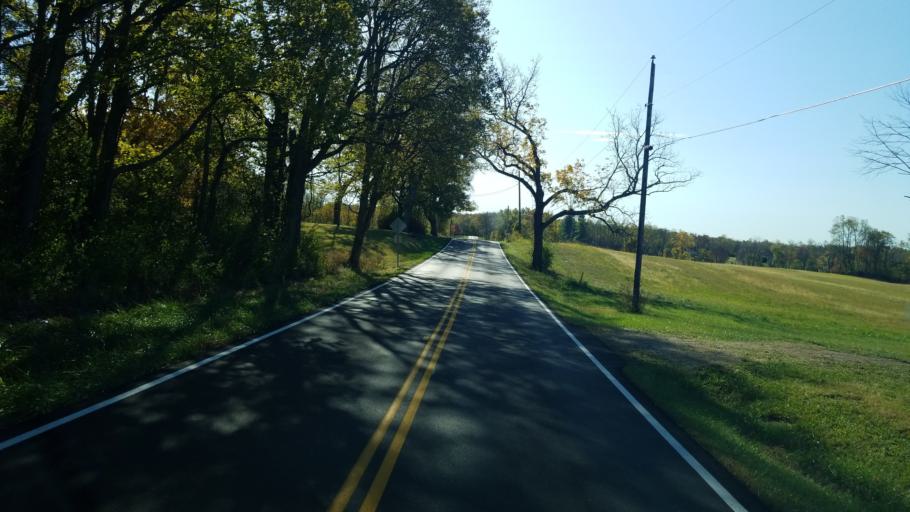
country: US
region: Ohio
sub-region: Warren County
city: Morrow
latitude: 39.3920
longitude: -84.0721
